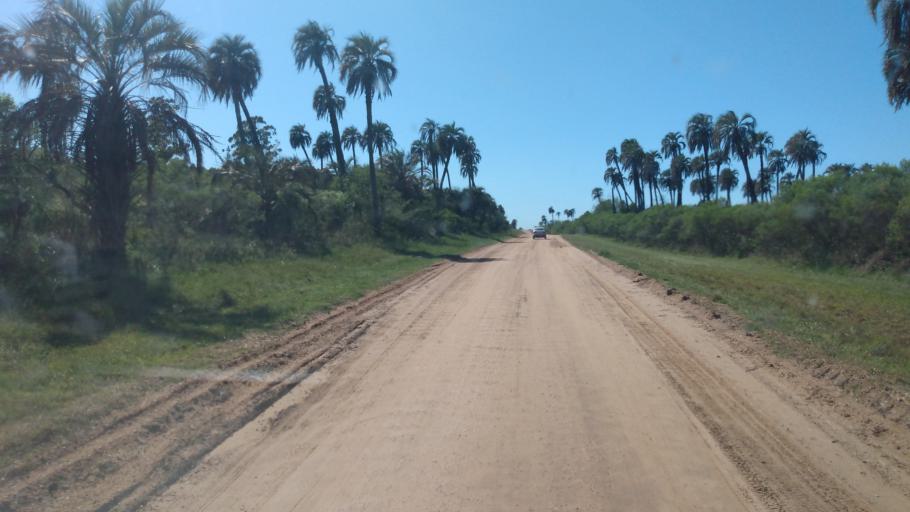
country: AR
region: Entre Rios
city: Ubajay
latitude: -31.8537
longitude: -58.2932
